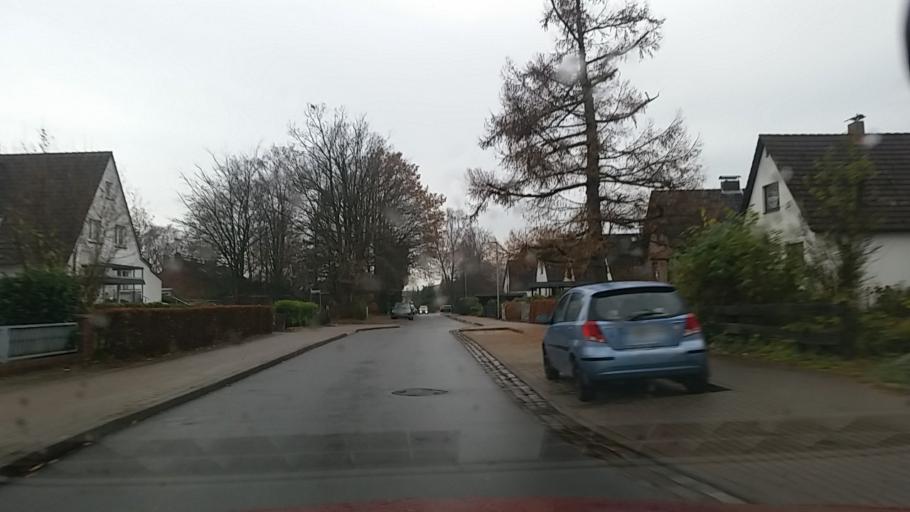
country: DE
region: Schleswig-Holstein
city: Barsbuettel
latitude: 53.5703
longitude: 10.1770
